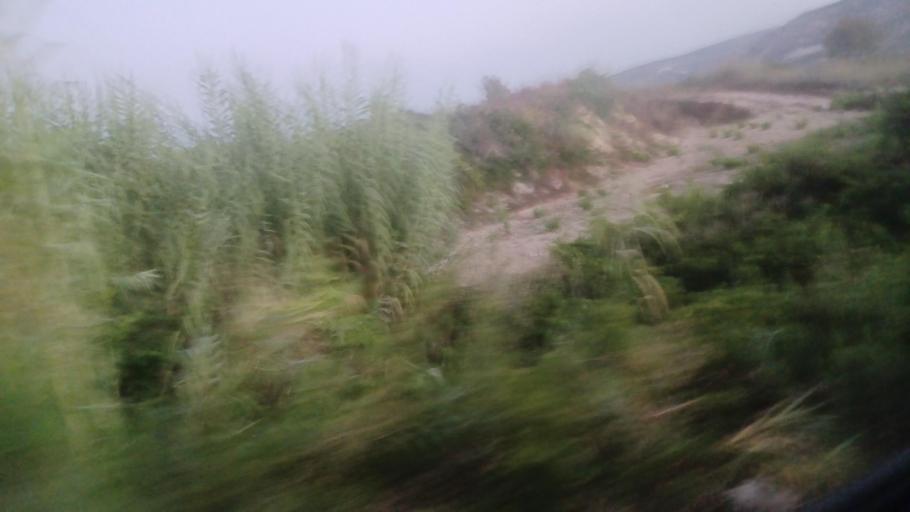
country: CY
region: Pafos
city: Tala
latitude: 34.8666
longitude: 32.4729
